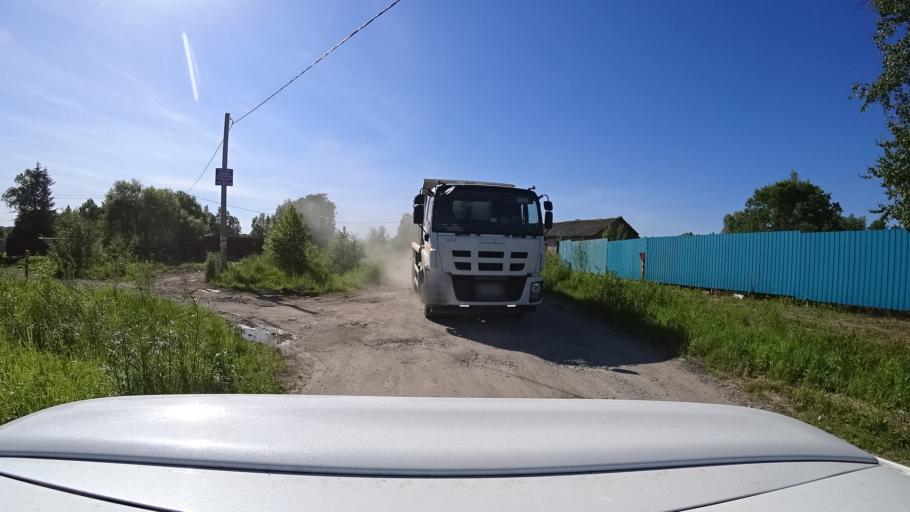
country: RU
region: Khabarovsk Krai
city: Topolevo
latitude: 48.5513
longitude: 135.1897
